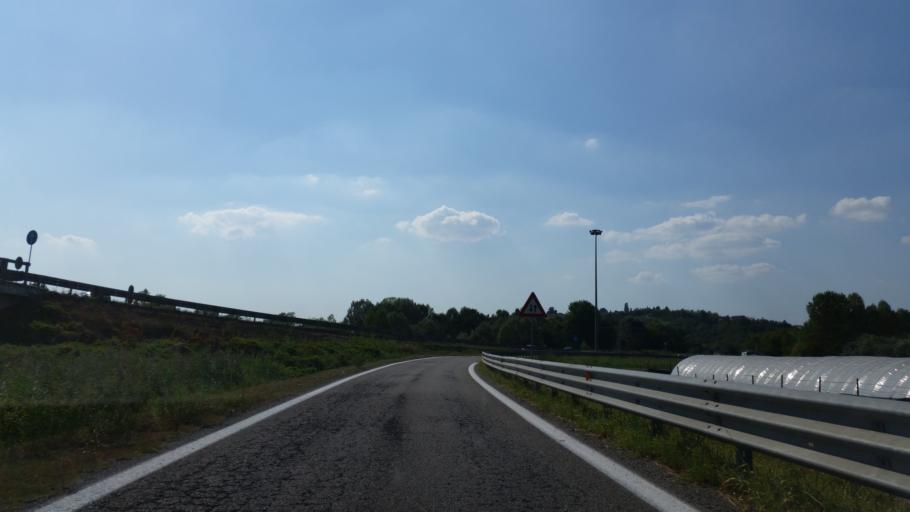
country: IT
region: Piedmont
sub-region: Provincia di Cuneo
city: Alba
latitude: 44.7078
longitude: 8.0224
